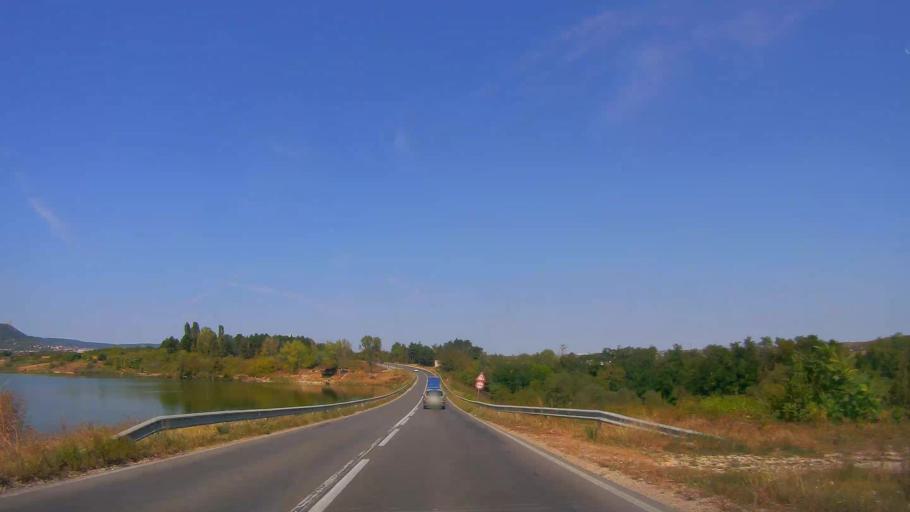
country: BG
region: Shumen
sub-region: Obshtina Shumen
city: Shumen
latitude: 43.2397
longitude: 26.9813
